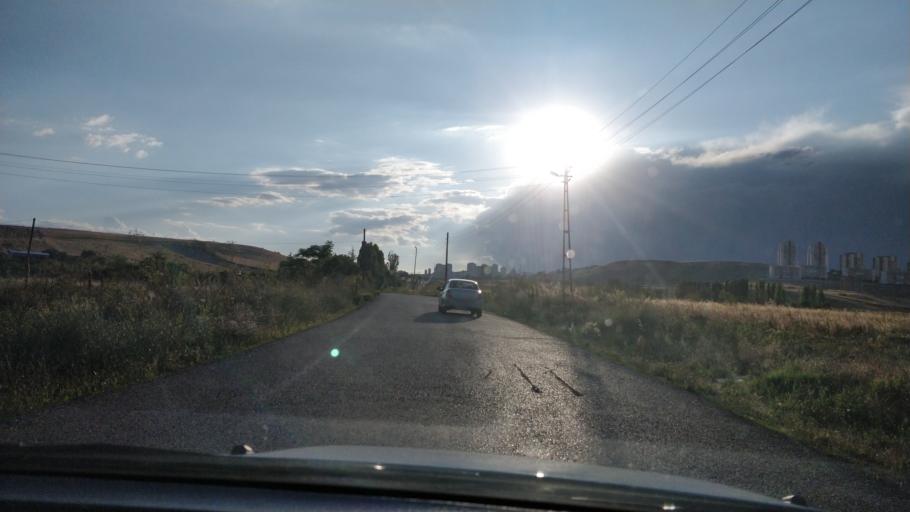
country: TR
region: Ankara
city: Etimesgut
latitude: 39.8257
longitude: 32.5715
